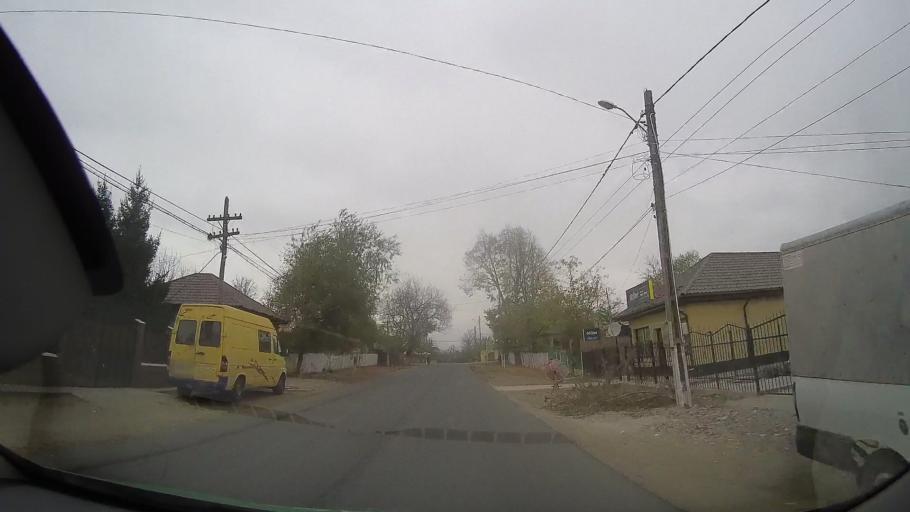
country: RO
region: Braila
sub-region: Comuna Ulmu
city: Ulmu
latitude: 44.9541
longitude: 27.3120
